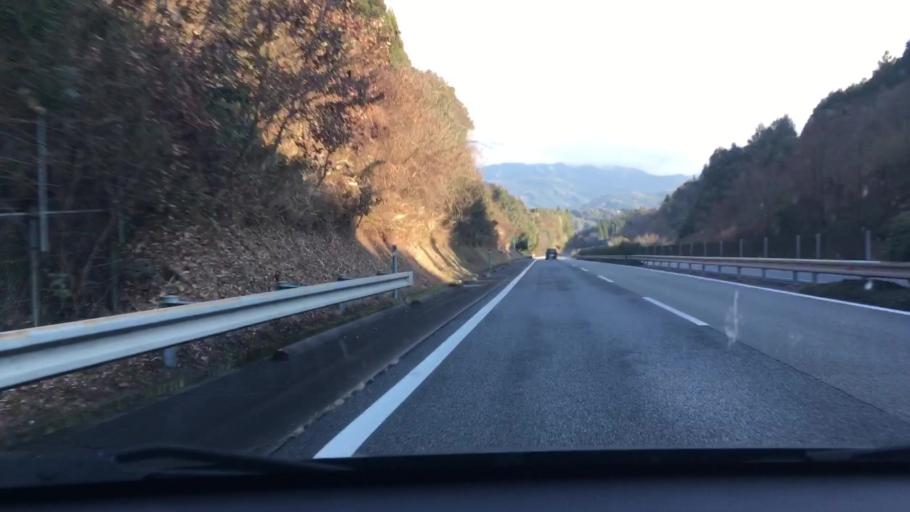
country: JP
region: Kumamoto
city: Hitoyoshi
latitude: 32.1819
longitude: 130.7821
